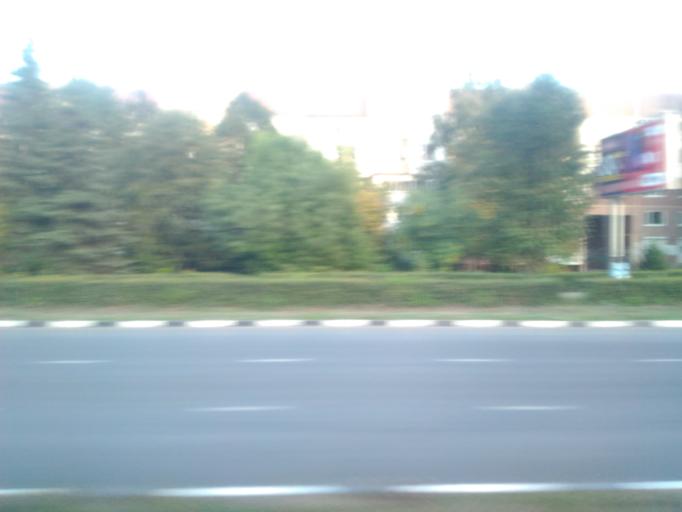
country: RU
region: Ulyanovsk
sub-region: Ulyanovskiy Rayon
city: Ulyanovsk
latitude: 54.2792
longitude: 48.2950
